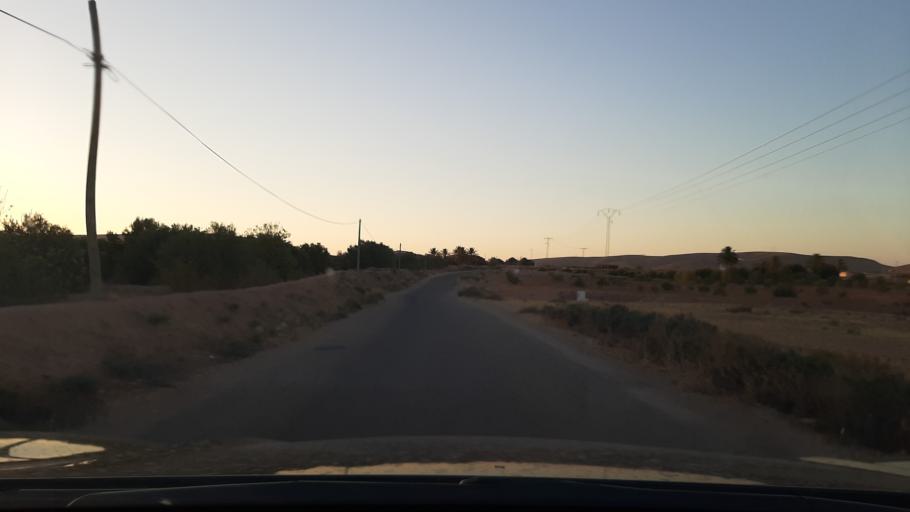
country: TN
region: Qabis
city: Matmata
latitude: 33.5567
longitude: 10.1848
